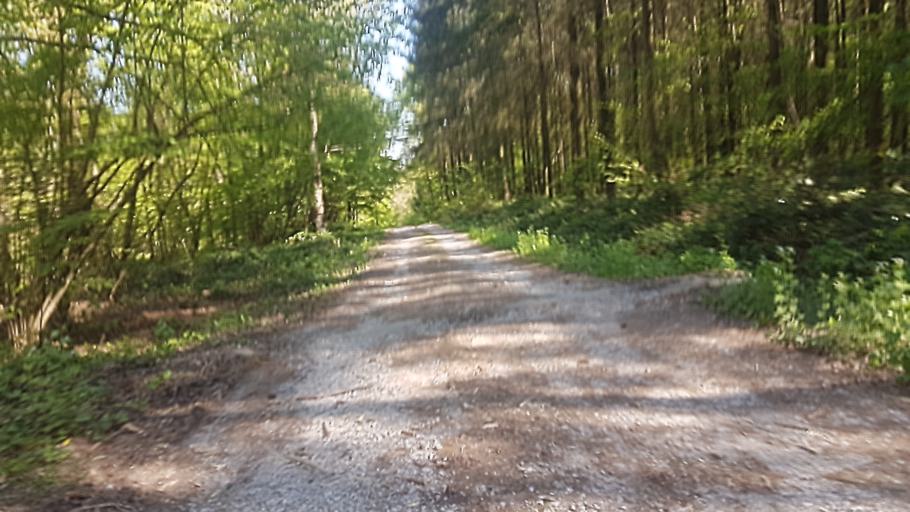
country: BE
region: Wallonia
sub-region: Province de Namur
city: Couvin
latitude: 50.0608
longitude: 4.5873
